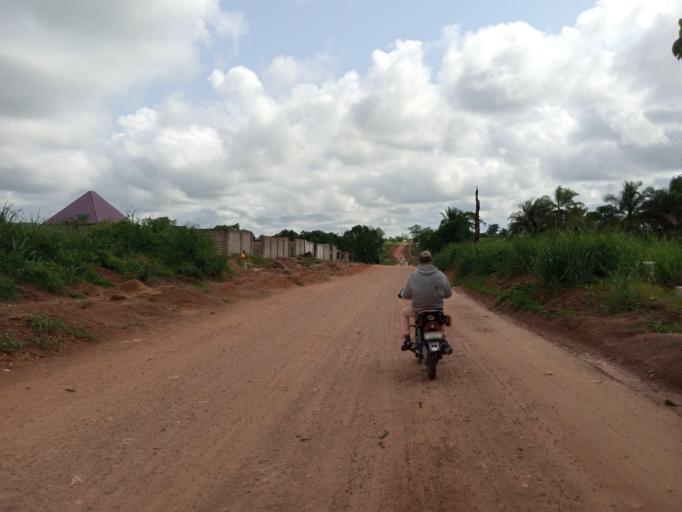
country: SL
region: Southern Province
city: Bo
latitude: 7.9854
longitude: -11.7374
